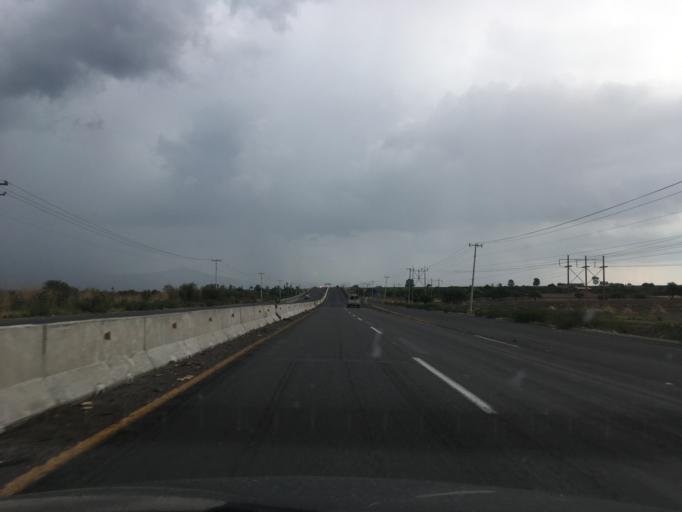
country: MX
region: Guanajuato
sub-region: Tarimoro
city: San Juan Bautista Cacalote
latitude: 20.3502
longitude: -100.8038
